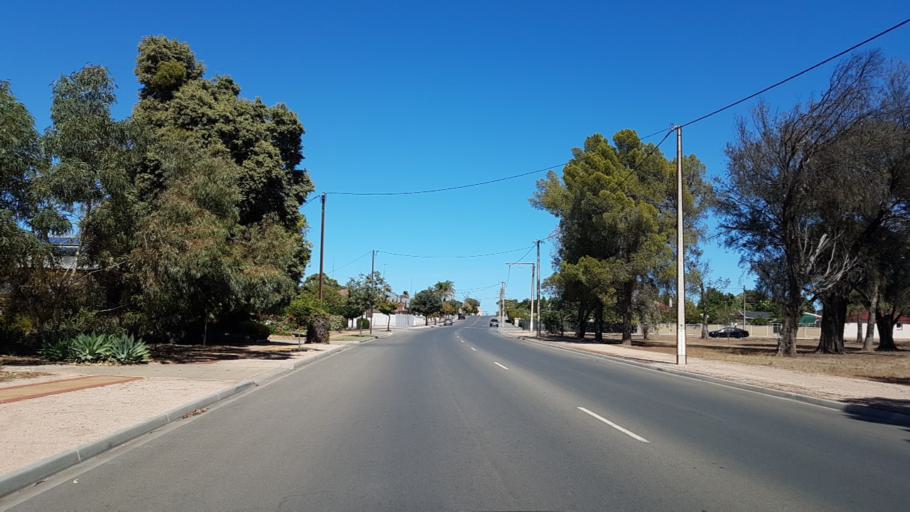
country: AU
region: South Australia
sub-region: Copper Coast
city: Kadina
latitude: -33.9611
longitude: 137.7229
